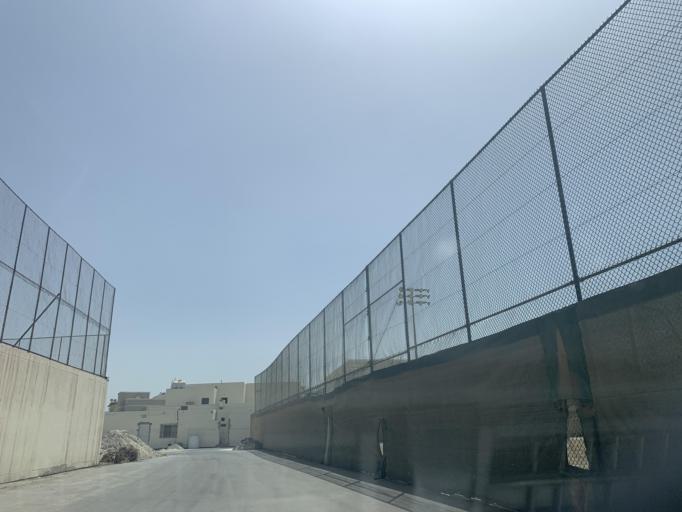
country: BH
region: Manama
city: Jidd Hafs
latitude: 26.2020
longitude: 50.5577
